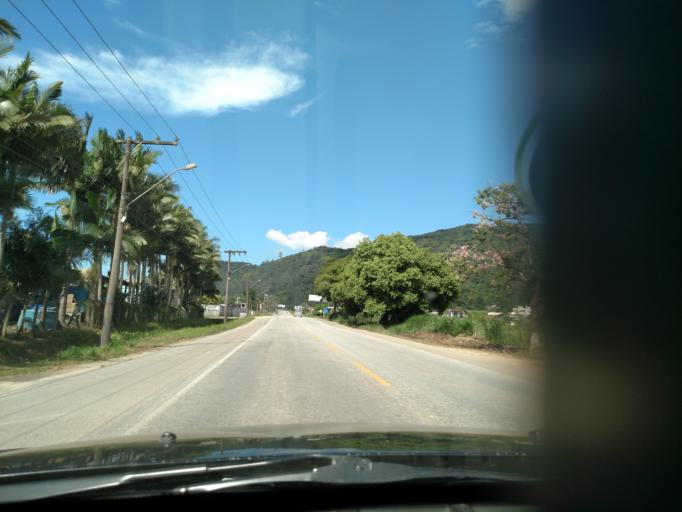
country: BR
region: Santa Catarina
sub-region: Itajai
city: Itajai
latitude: -26.8920
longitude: -48.7659
